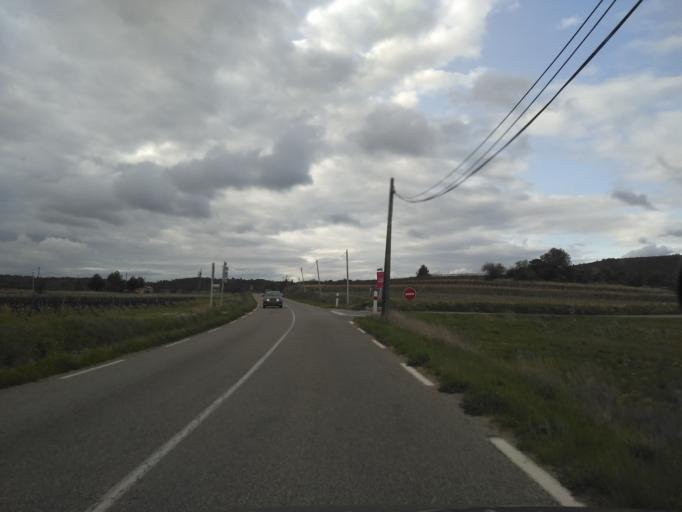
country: FR
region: Provence-Alpes-Cote d'Azur
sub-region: Departement du Var
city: Barjols
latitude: 43.5854
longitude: 6.0151
